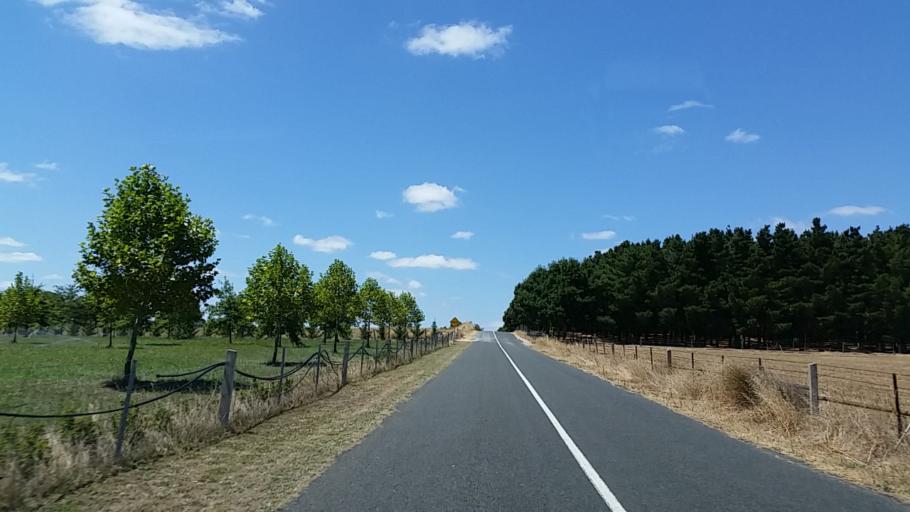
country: AU
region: South Australia
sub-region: Adelaide Hills
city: Lobethal
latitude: -34.9057
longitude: 138.8911
